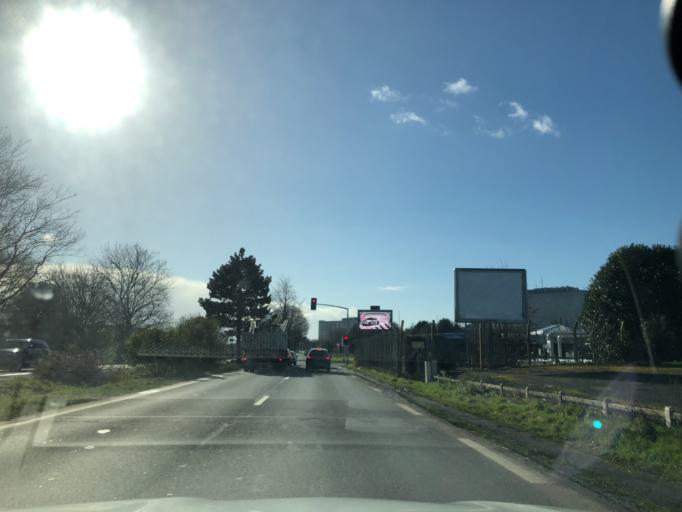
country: FR
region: Lower Normandy
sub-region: Departement du Calvados
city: Caen
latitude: 49.2080
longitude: -0.3476
